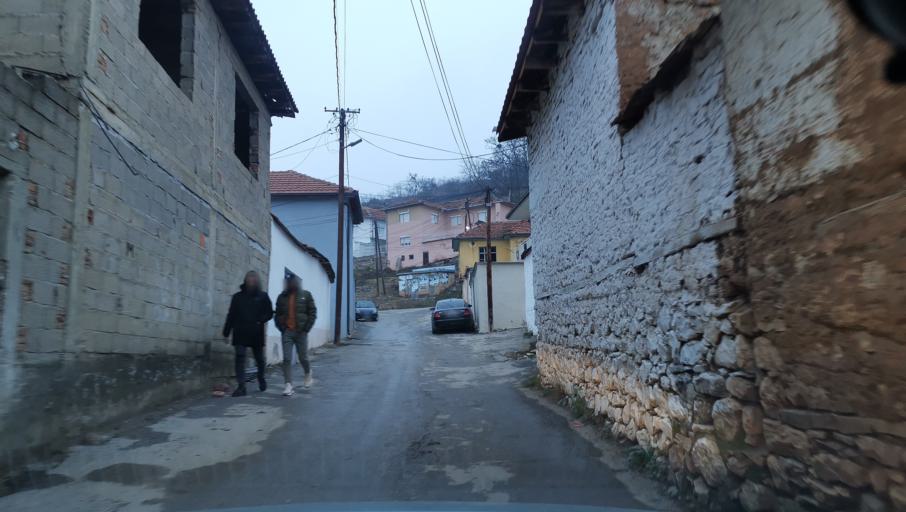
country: MK
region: Debar
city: Debar
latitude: 41.5245
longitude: 20.5277
